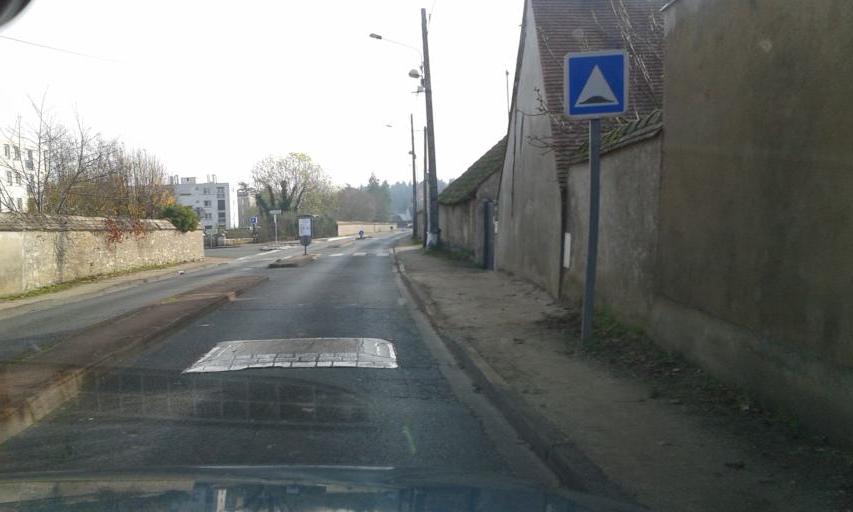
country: FR
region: Centre
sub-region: Departement du Loiret
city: Olivet
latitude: 47.8529
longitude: 1.9239
